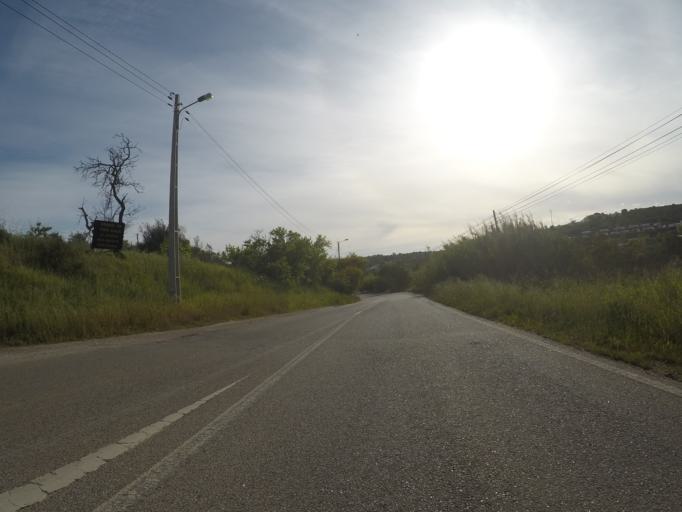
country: PT
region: Faro
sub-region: Lagos
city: Lagos
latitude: 37.1007
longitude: -8.7153
